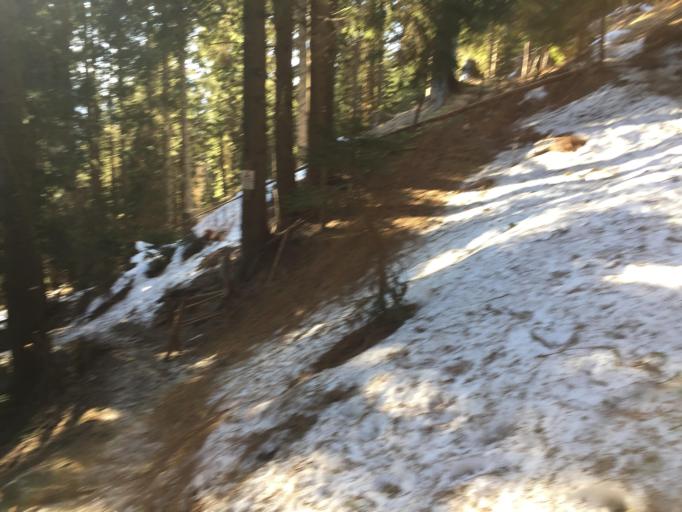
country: IT
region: Friuli Venezia Giulia
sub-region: Provincia di Udine
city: Malborghetto
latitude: 46.5508
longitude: 13.4996
